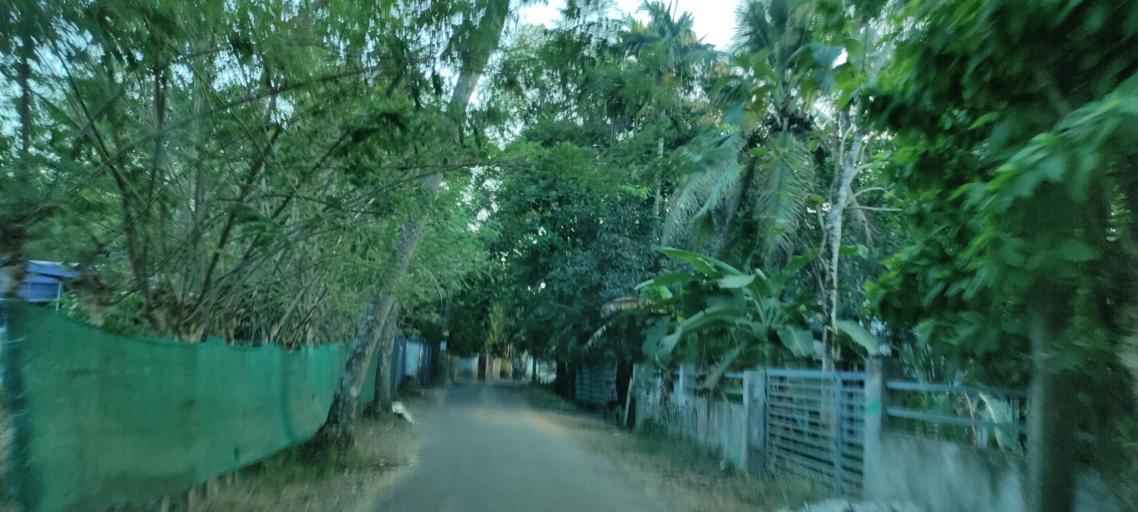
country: IN
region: Kerala
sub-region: Alappuzha
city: Alleppey
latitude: 9.5372
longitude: 76.3343
